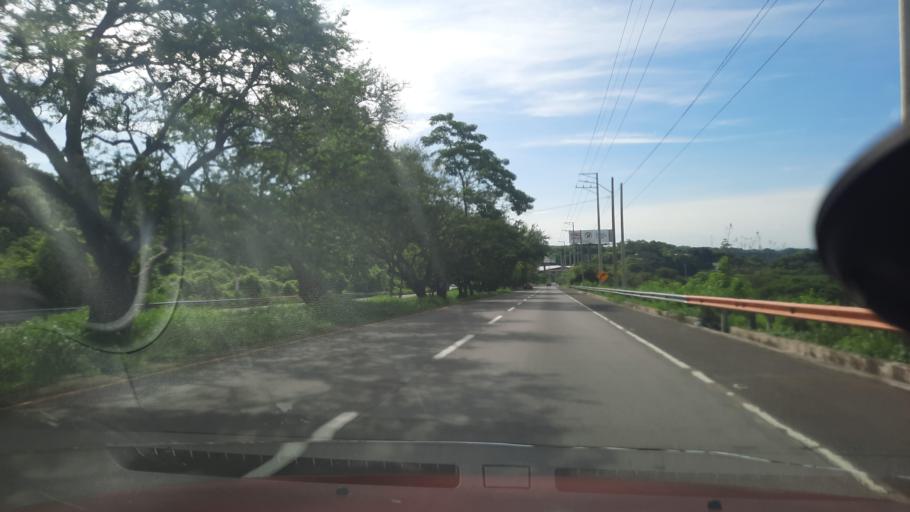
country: SV
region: La Paz
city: Olocuilta
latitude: 13.5250
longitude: -89.1089
